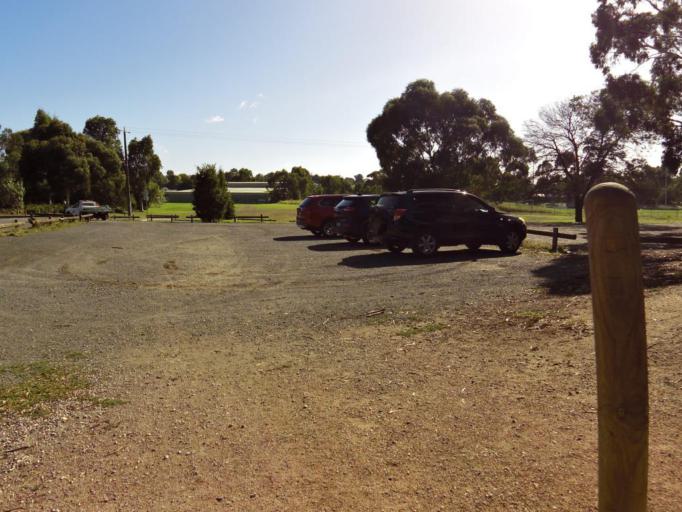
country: AU
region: Victoria
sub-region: Maroondah
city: Bayswater North
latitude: -37.8061
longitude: 145.2913
